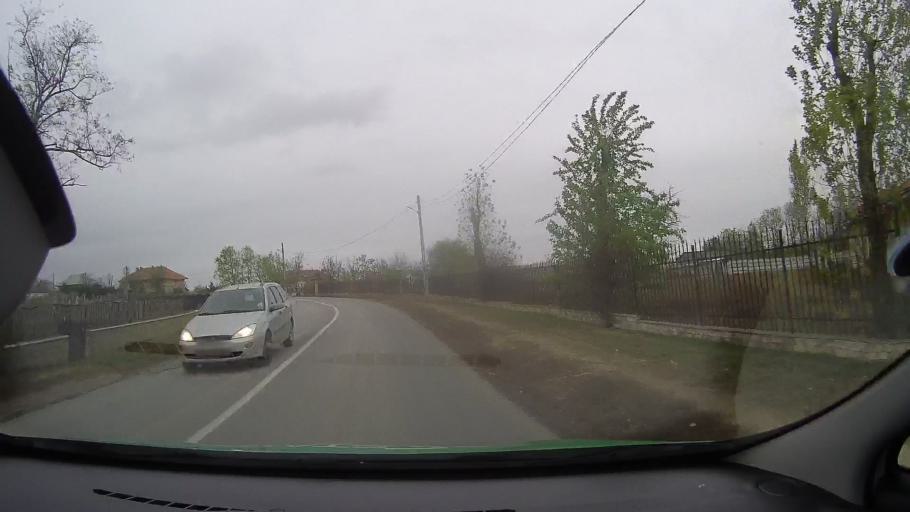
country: RO
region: Constanta
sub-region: Comuna Pantelimon
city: Pantelimon
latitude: 44.5477
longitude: 28.3293
